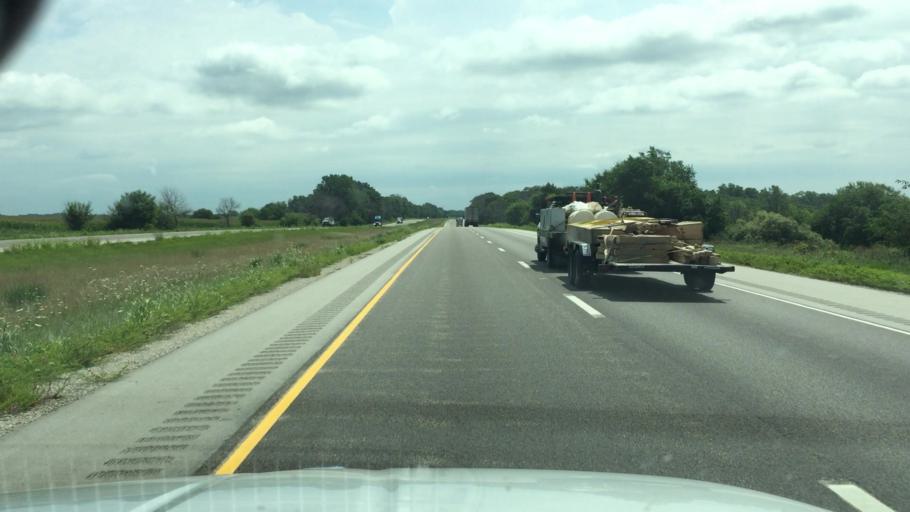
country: US
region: Illinois
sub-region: Peoria County
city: Elmwood
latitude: 40.8688
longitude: -90.0384
